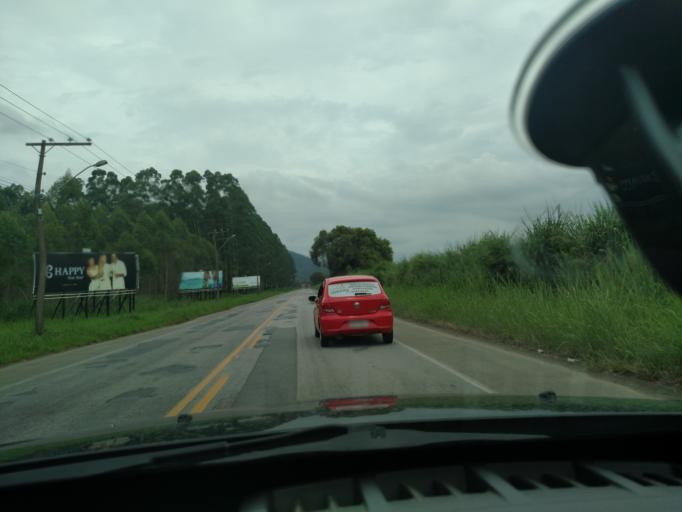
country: BR
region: Santa Catarina
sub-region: Itajai
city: Itajai
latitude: -26.8810
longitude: -48.7777
